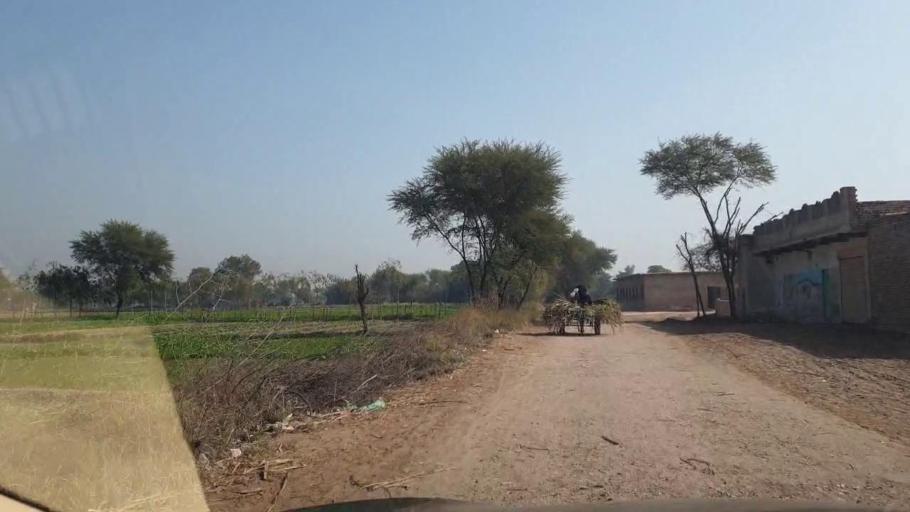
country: PK
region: Sindh
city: Ubauro
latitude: 28.1103
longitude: 69.7710
